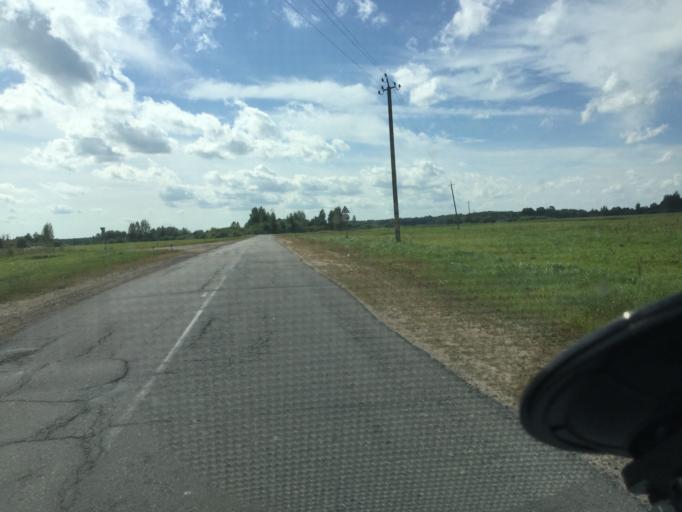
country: BY
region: Vitebsk
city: Chashniki
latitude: 55.3132
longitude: 29.4194
